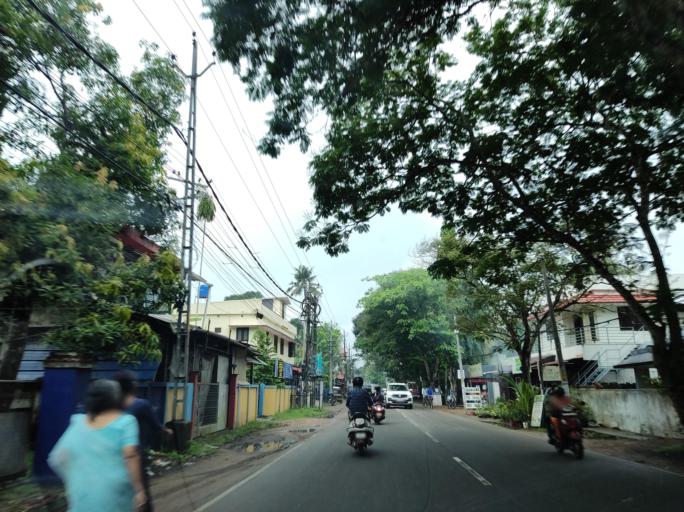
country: IN
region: Kerala
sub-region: Alappuzha
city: Mavelikara
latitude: 9.2459
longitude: 76.5203
